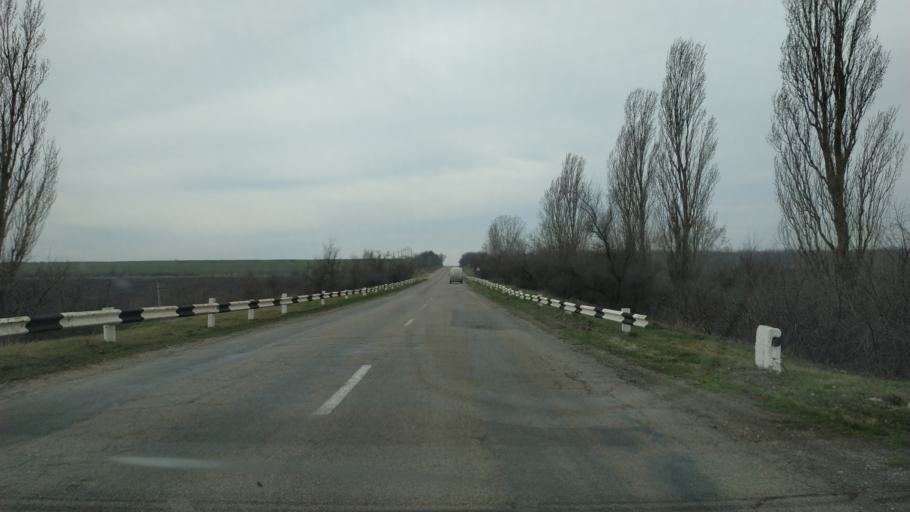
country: MD
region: Cahul
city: Cahul
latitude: 45.9590
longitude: 28.3790
